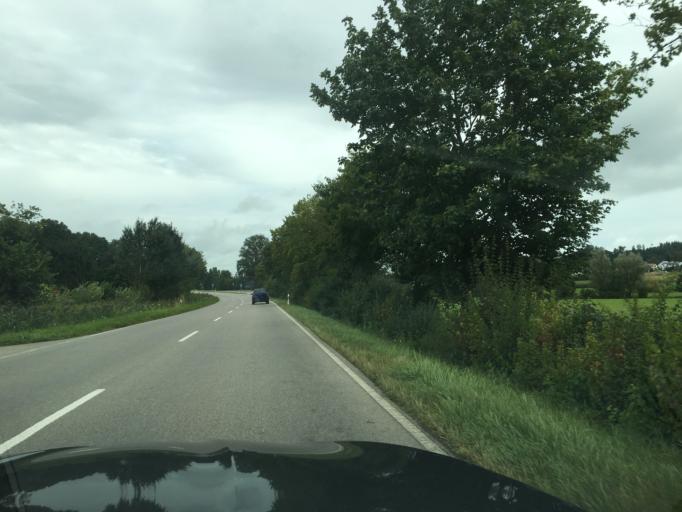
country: DE
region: Bavaria
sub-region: Swabia
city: Altenmunster
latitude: 48.4542
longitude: 10.5882
